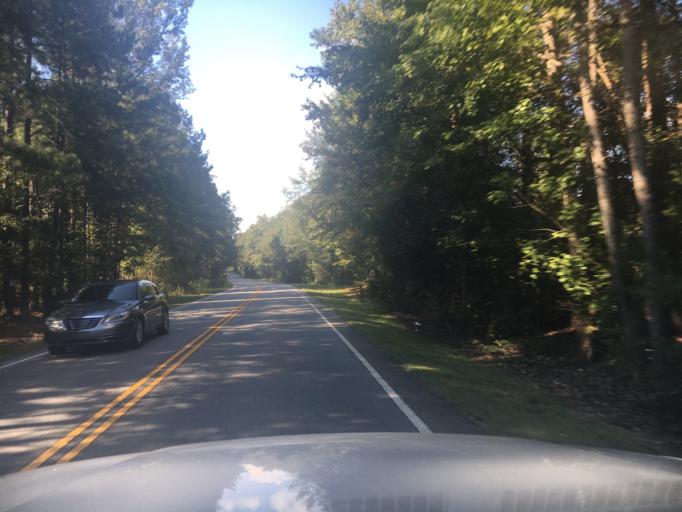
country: US
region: South Carolina
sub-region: Greenville County
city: Fountain Inn
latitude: 34.6179
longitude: -82.2378
